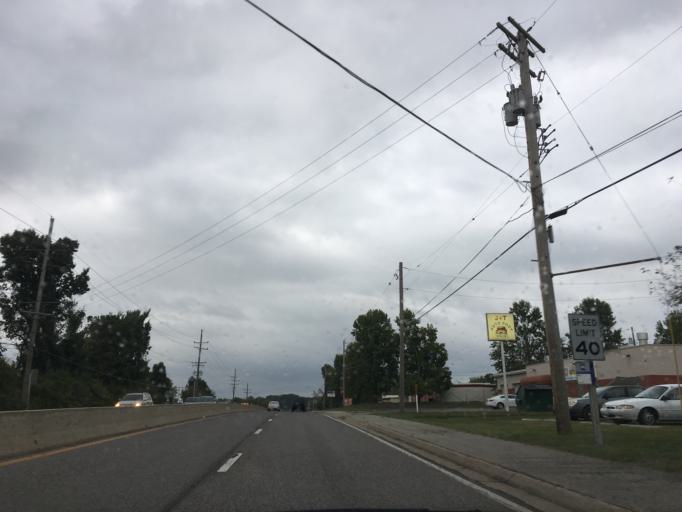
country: US
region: Missouri
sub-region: Saint Louis County
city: Maryland Heights
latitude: 38.7149
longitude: -90.4081
